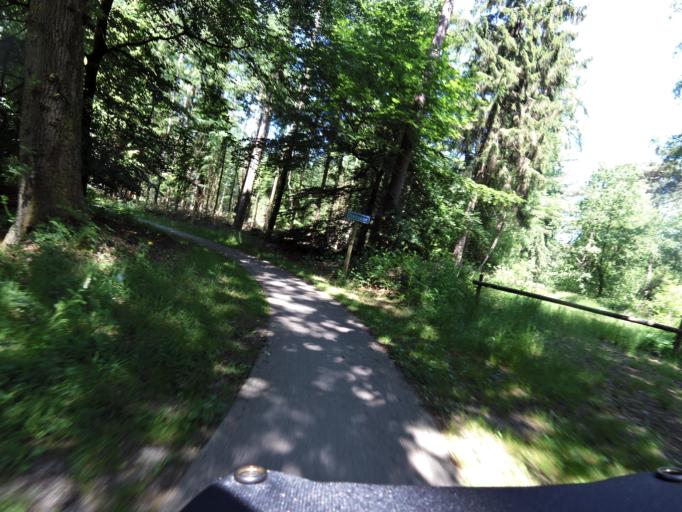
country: NL
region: Overijssel
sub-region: Gemeente Twenterand
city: Den Ham
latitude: 52.4883
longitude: 6.4687
